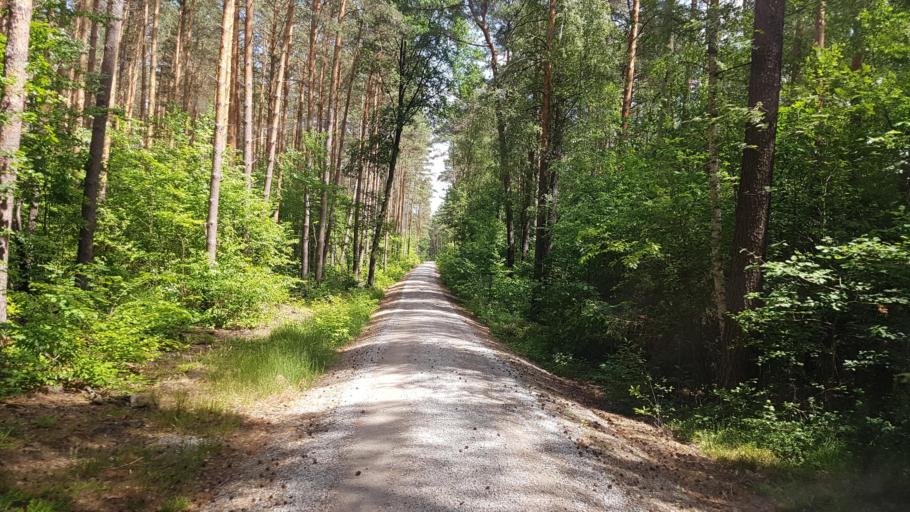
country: DE
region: Brandenburg
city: Plessa
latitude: 51.4955
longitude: 13.5955
